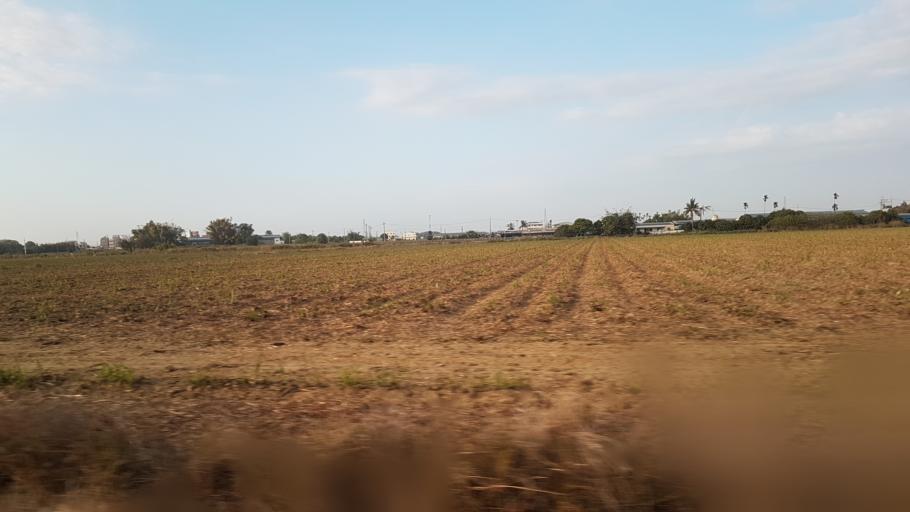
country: TW
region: Taiwan
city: Xinying
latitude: 23.3467
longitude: 120.3717
